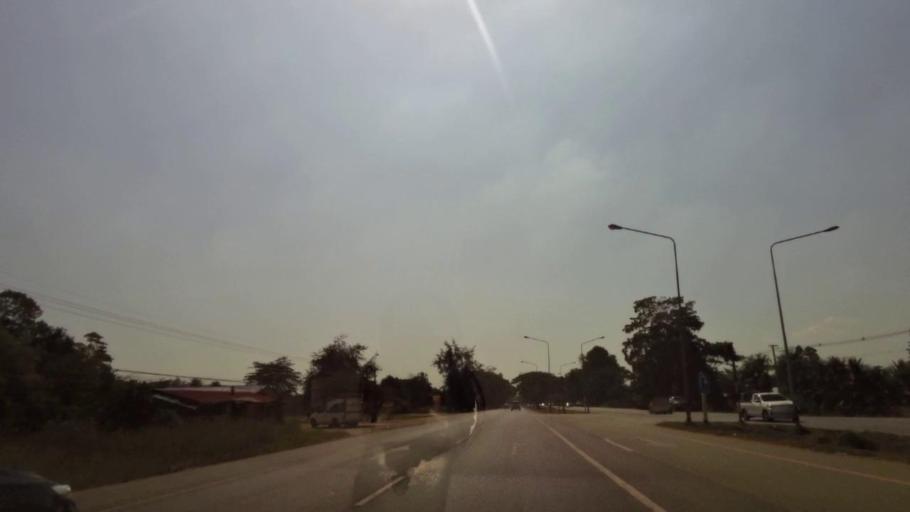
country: TH
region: Phichit
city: Wachira Barami
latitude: 16.3720
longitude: 100.1331
